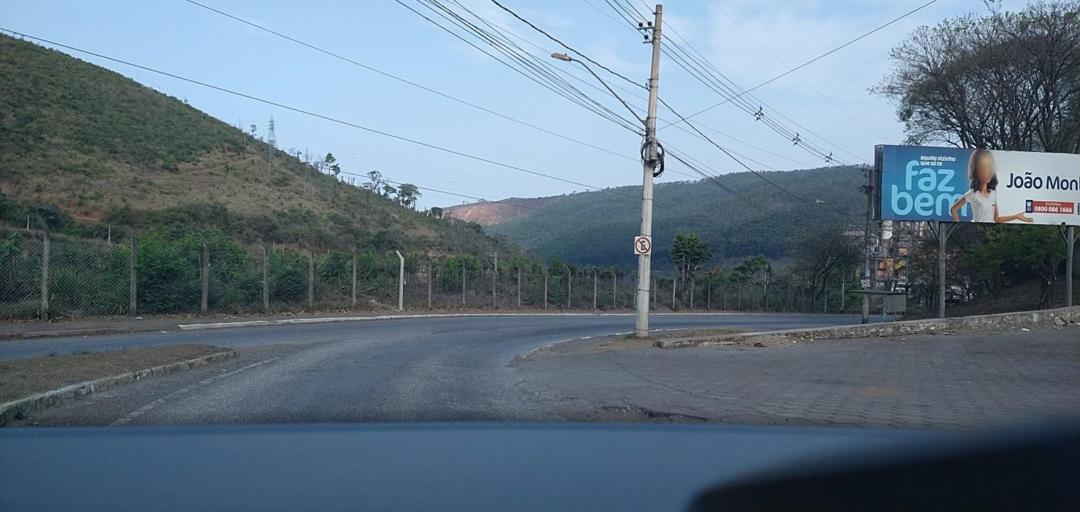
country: BR
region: Minas Gerais
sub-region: Joao Monlevade
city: Joao Monlevade
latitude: -19.8210
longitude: -43.1328
